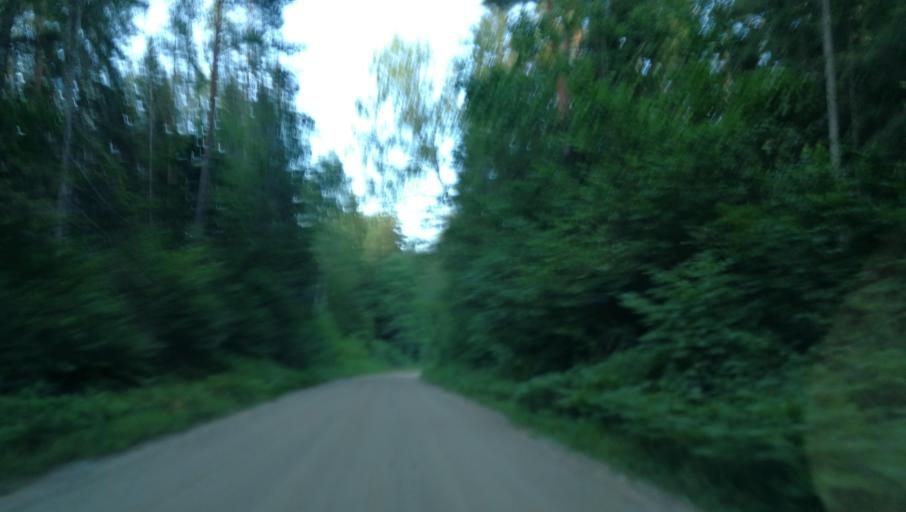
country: LV
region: Cesu Rajons
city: Cesis
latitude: 57.3492
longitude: 25.1920
